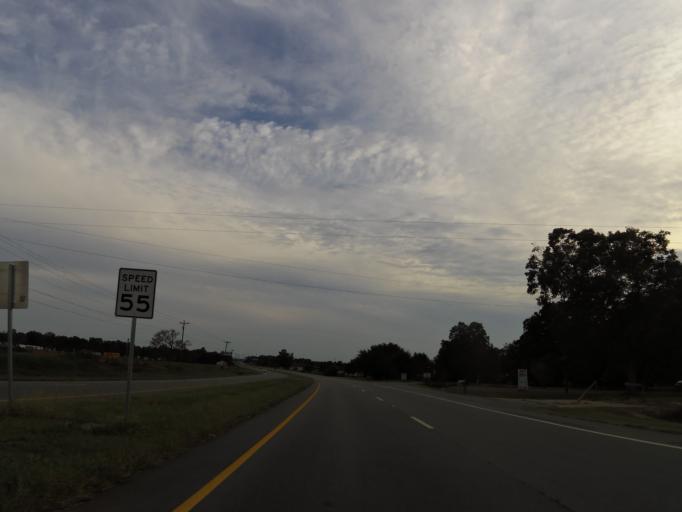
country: US
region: Alabama
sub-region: Escambia County
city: Atmore
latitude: 31.1004
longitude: -87.4799
